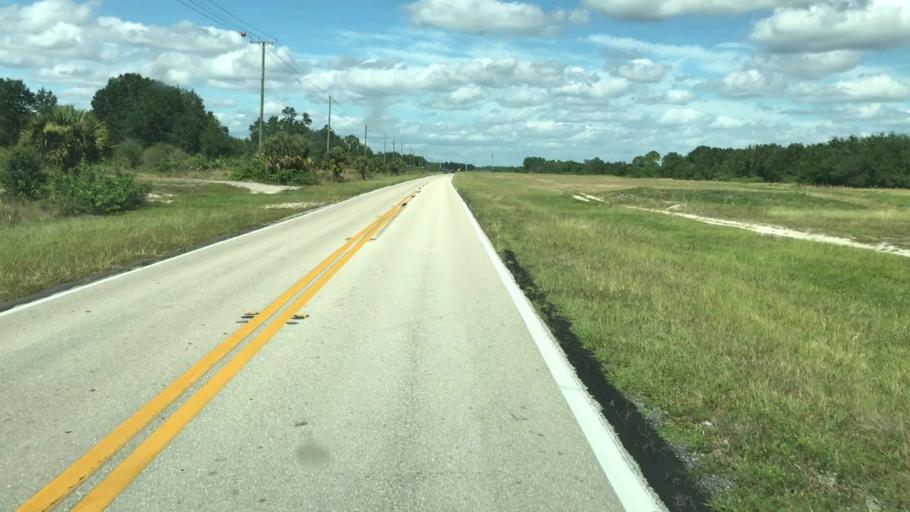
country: US
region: Florida
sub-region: Lee County
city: Lehigh Acres
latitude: 26.6707
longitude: -81.6637
